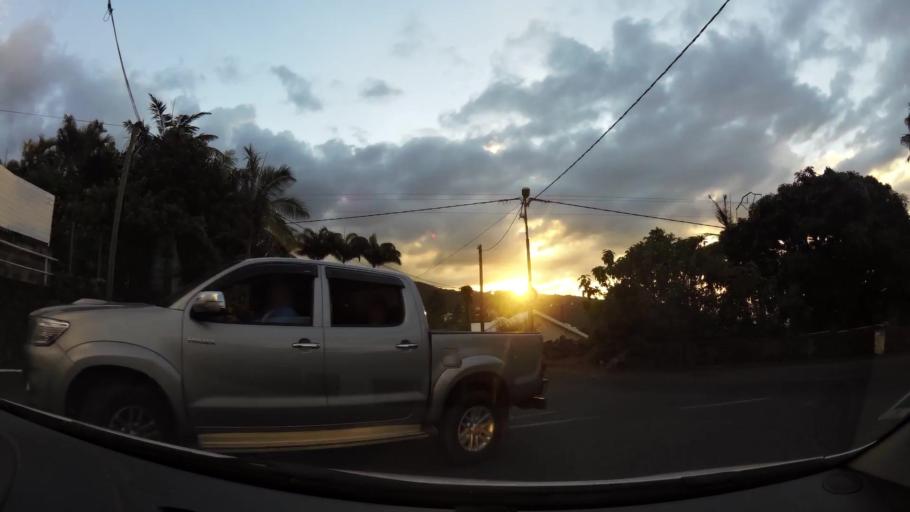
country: RE
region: Reunion
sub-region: Reunion
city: Saint-Denis
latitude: -20.9093
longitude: 55.4623
